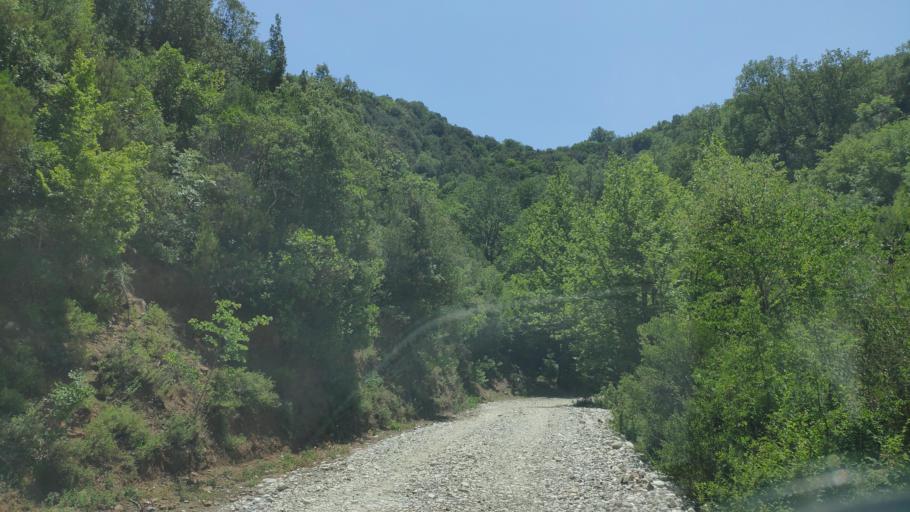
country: GR
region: Epirus
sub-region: Nomos Artas
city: Ano Kalentini
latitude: 39.1774
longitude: 21.3624
